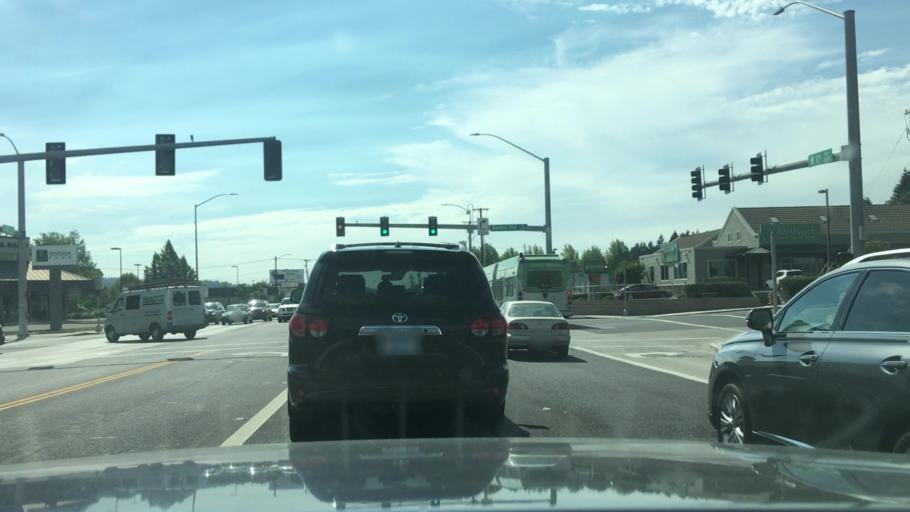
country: US
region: Oregon
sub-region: Lane County
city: Eugene
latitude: 44.0481
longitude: -123.1475
